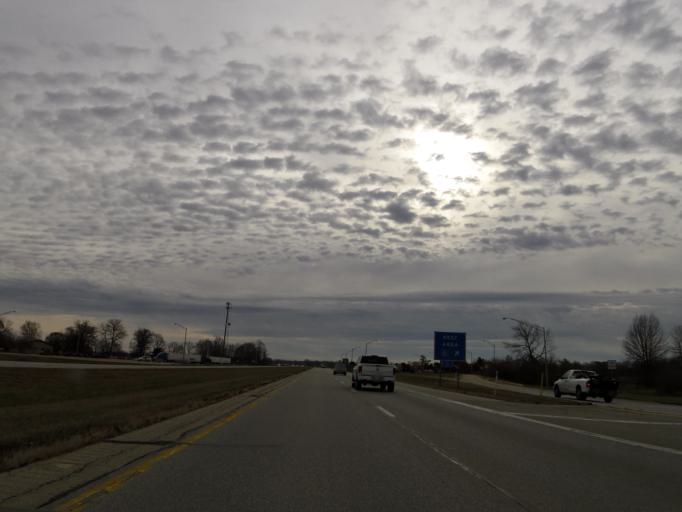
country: US
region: Indiana
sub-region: Hendricks County
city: Pittsboro
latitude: 39.9023
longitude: -86.5567
